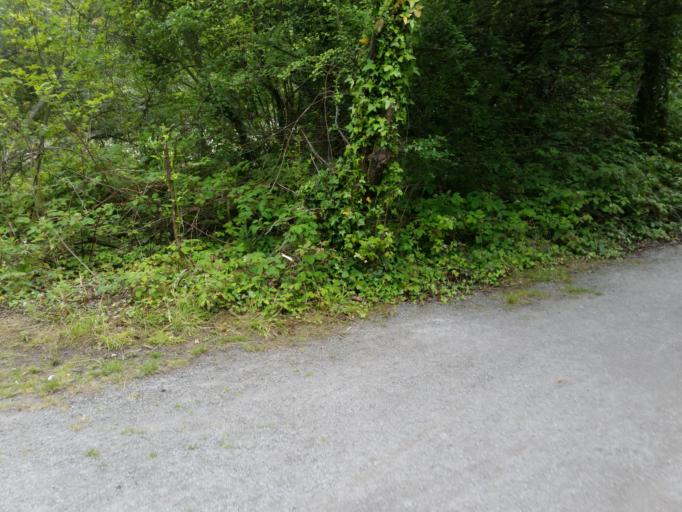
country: GB
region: Northern Ireland
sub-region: Castlereagh District
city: Castlereagh
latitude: 54.6092
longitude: -5.8871
